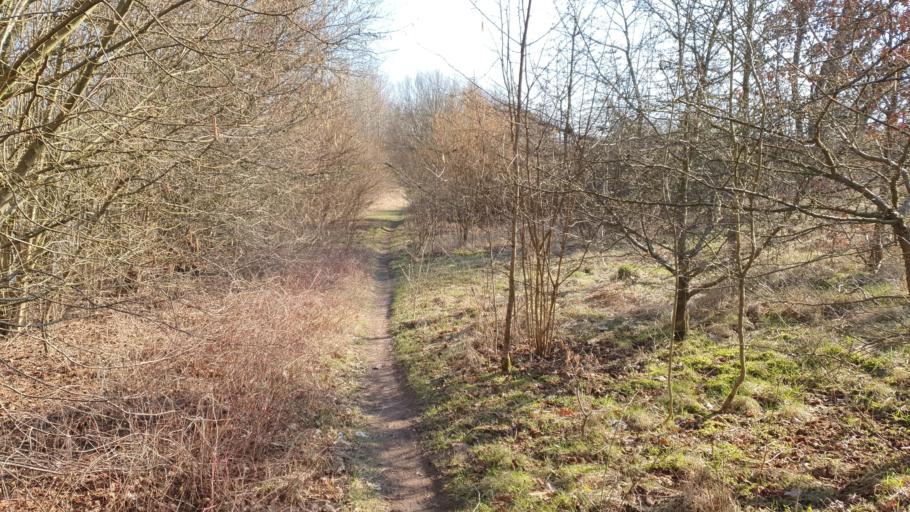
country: DE
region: Mecklenburg-Vorpommern
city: Wittenforden
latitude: 53.6324
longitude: 11.3485
